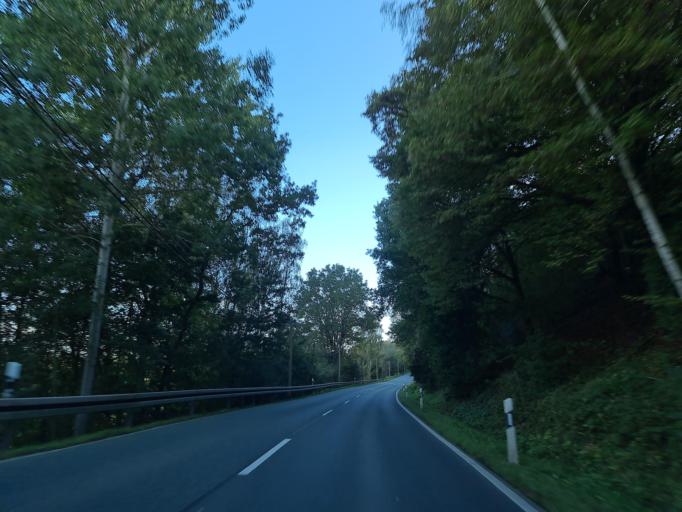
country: DE
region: Thuringia
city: Wunschendorf
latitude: 50.8122
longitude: 12.0753
